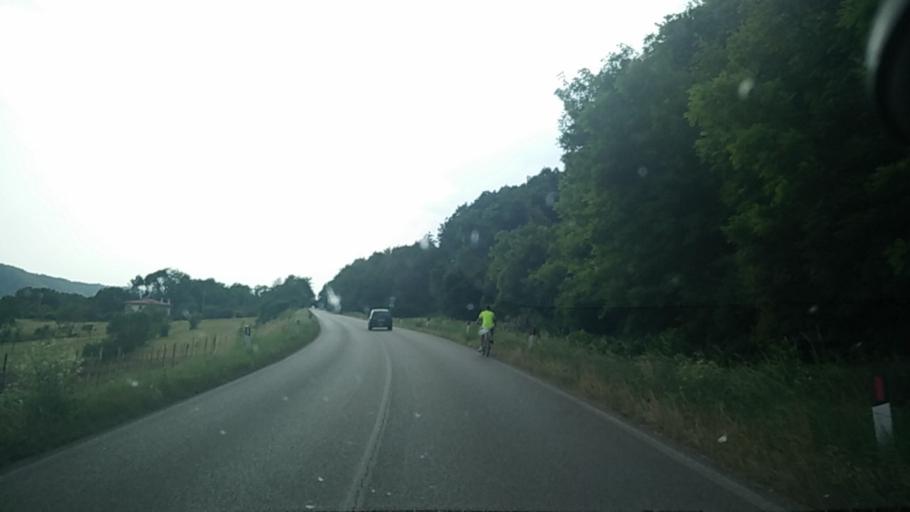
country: IT
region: Veneto
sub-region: Provincia di Treviso
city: Cison di Valmarino
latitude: 45.9710
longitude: 12.1584
